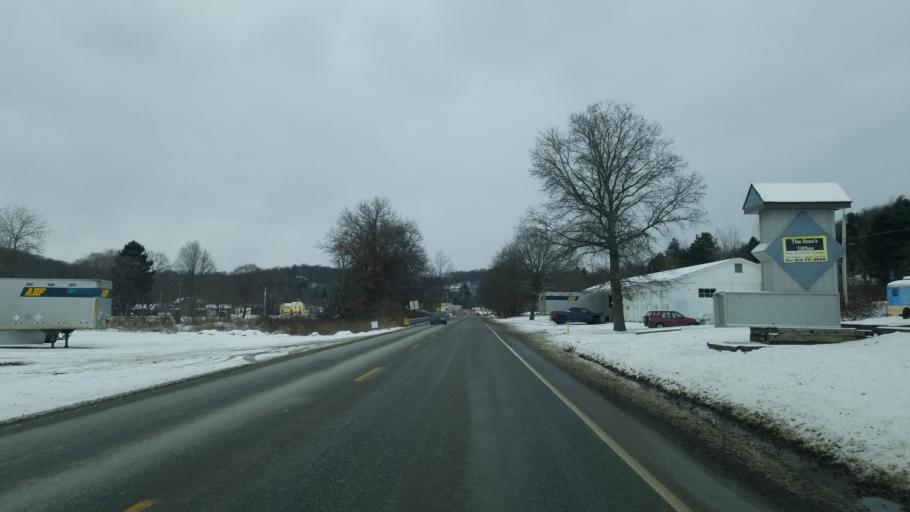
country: US
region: Pennsylvania
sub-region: Clearfield County
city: Sandy
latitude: 41.0883
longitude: -78.7676
